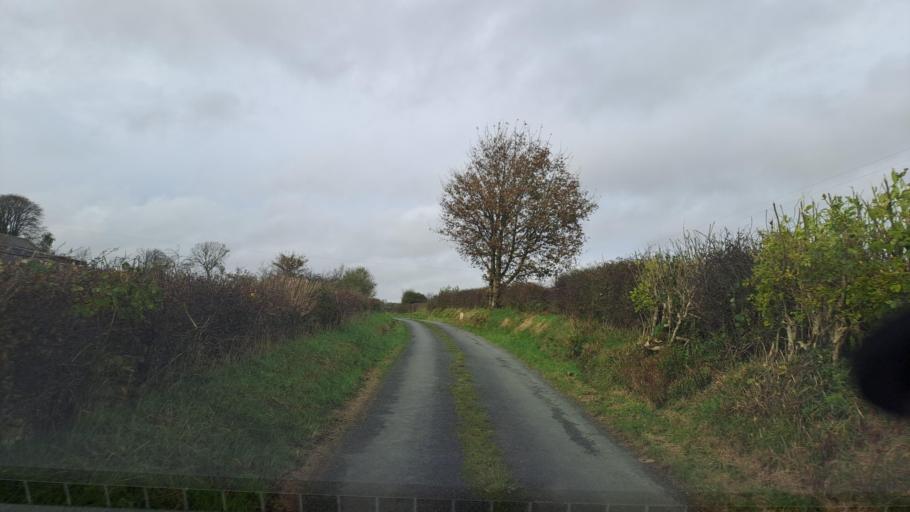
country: IE
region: Ulster
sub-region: County Monaghan
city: Carrickmacross
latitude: 54.0091
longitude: -6.7935
